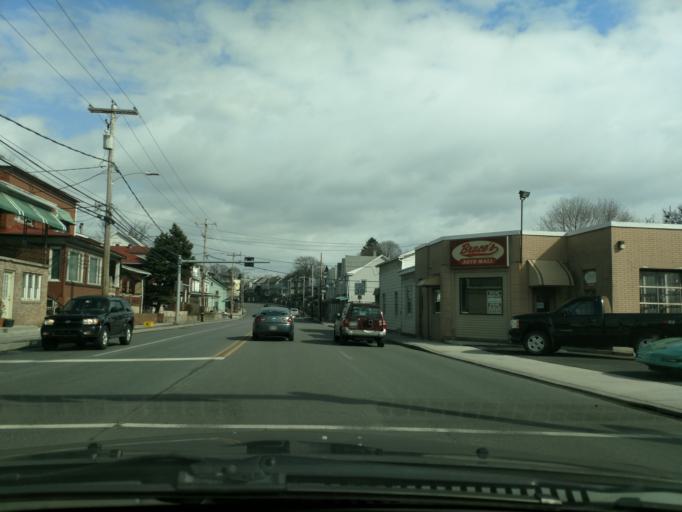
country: US
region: Pennsylvania
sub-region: Schuylkill County
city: Schuylkill Haven
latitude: 40.6377
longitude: -76.1756
